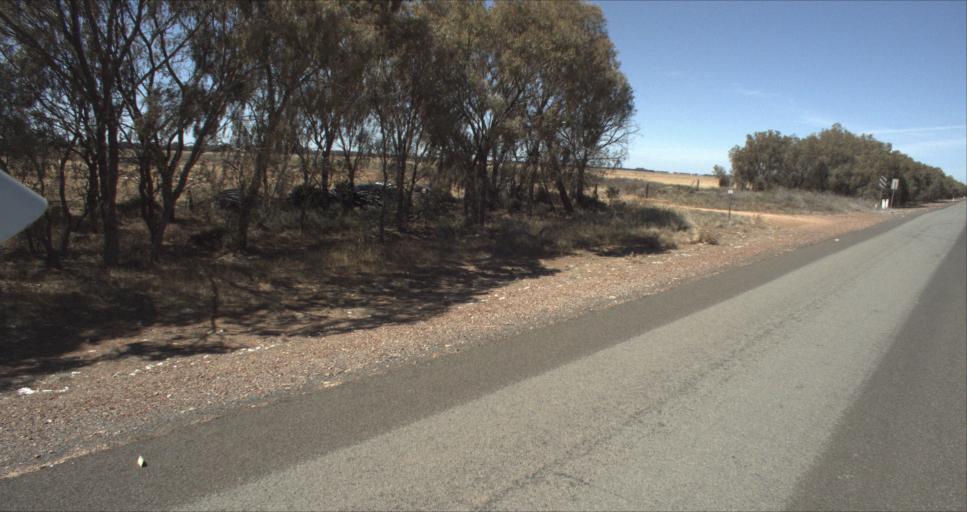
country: AU
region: New South Wales
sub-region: Leeton
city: Leeton
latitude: -34.4817
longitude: 146.2904
